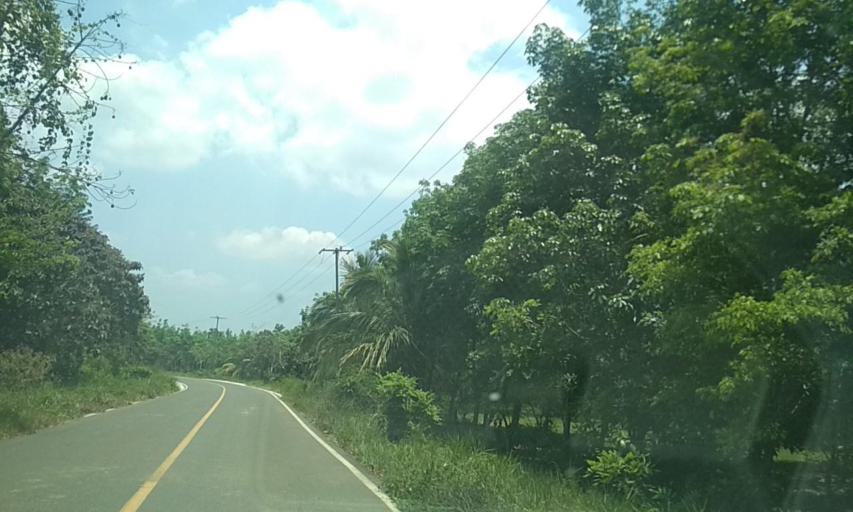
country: MX
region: Tabasco
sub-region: Huimanguillo
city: Francisco Rueda
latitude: 17.7492
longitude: -94.0408
